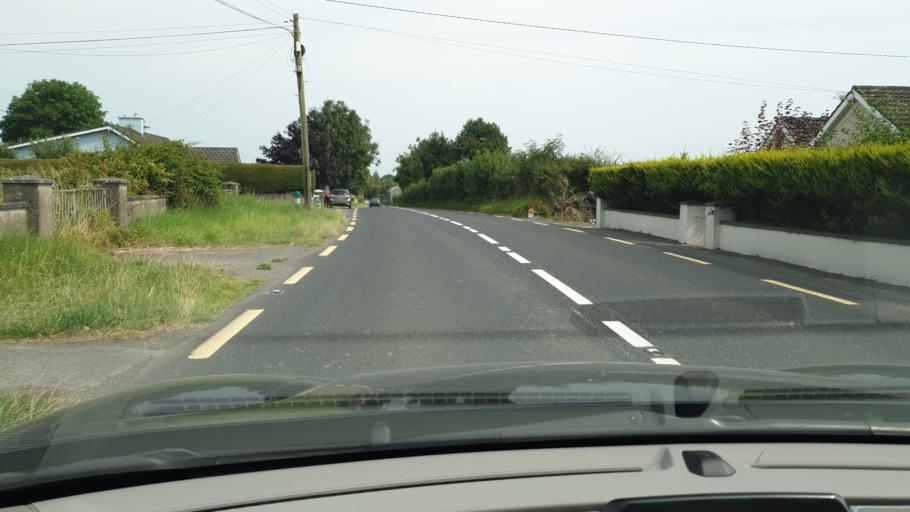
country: IE
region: Leinster
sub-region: An Mhi
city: Kells
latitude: 53.7139
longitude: -6.9007
